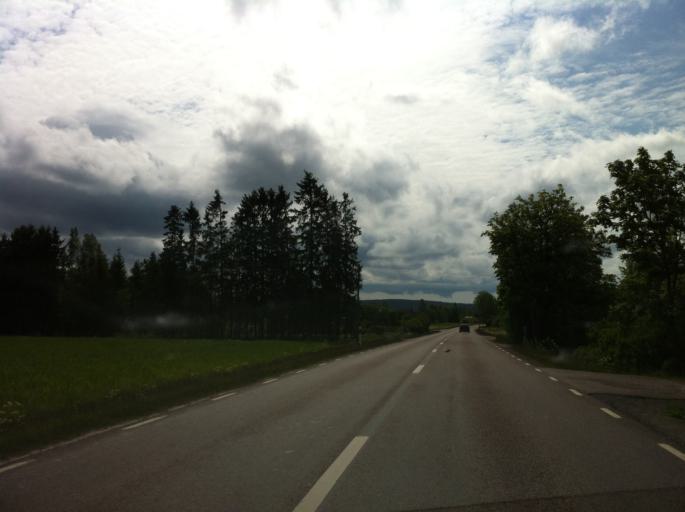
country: SE
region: Vaermland
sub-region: Sunne Kommun
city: Sunne
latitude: 59.6727
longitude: 13.1469
